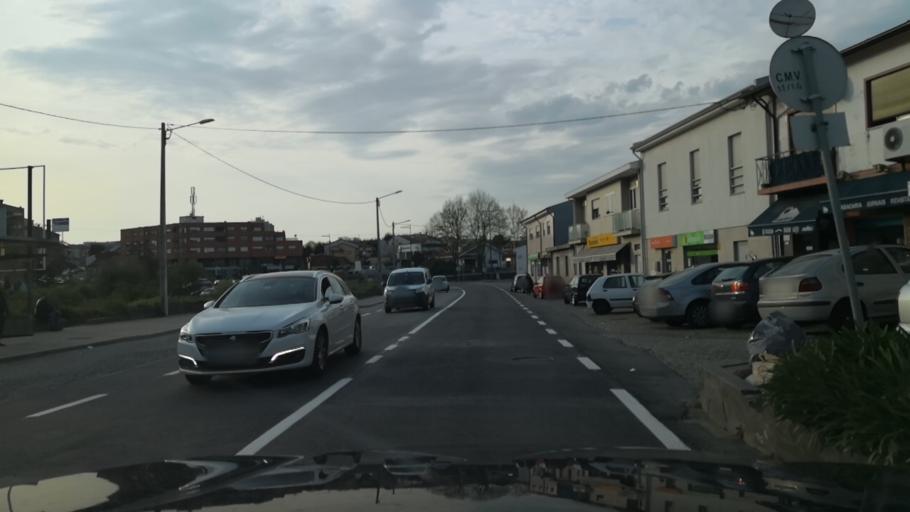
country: PT
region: Porto
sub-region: Valongo
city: Valongo
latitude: 41.1869
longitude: -8.4884
